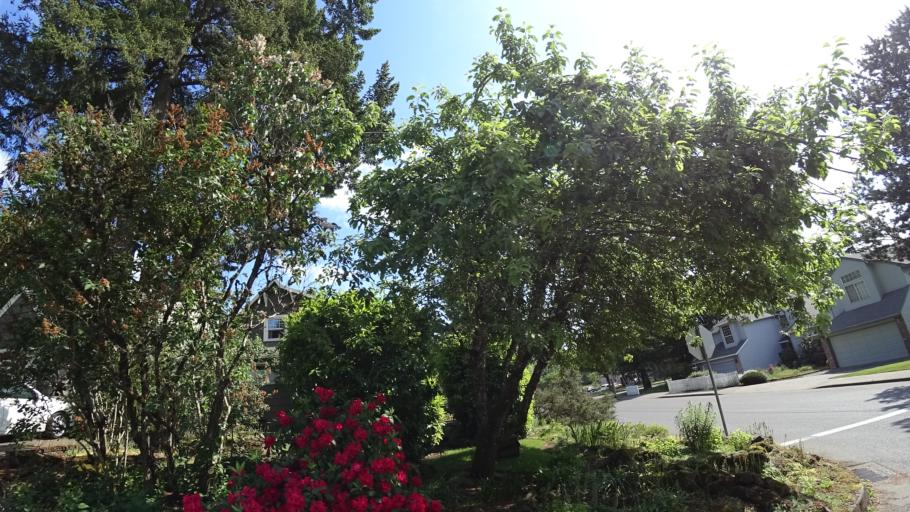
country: US
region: Oregon
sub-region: Washington County
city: Garden Home-Whitford
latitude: 45.4690
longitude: -122.7179
